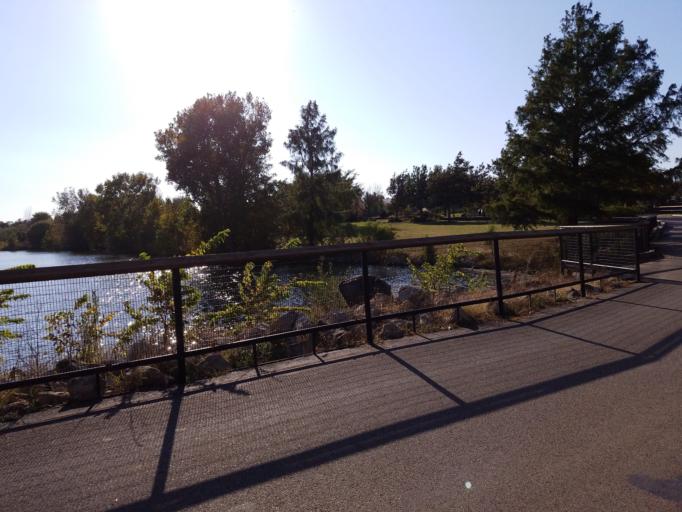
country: US
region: Kansas
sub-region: Saline County
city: Salina
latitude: 38.8558
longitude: -97.7636
